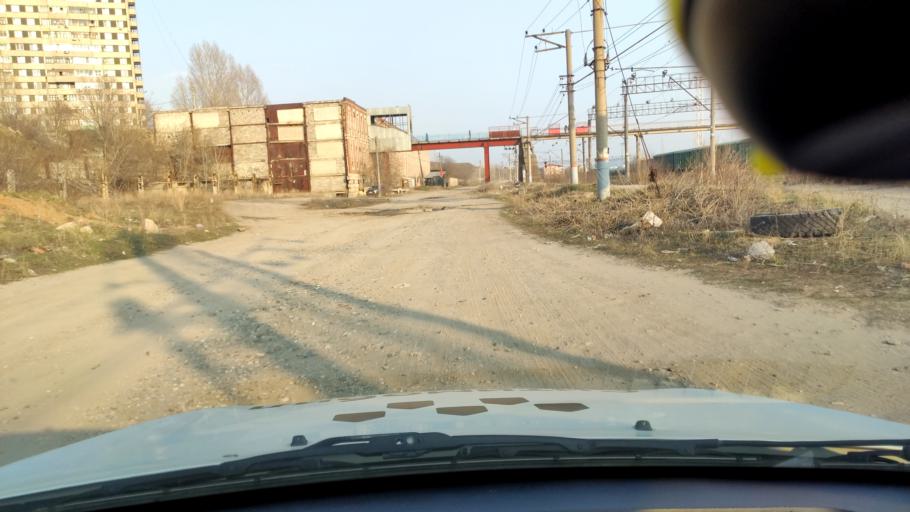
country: RU
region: Samara
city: Zhigulevsk
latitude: 53.4796
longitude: 49.5236
